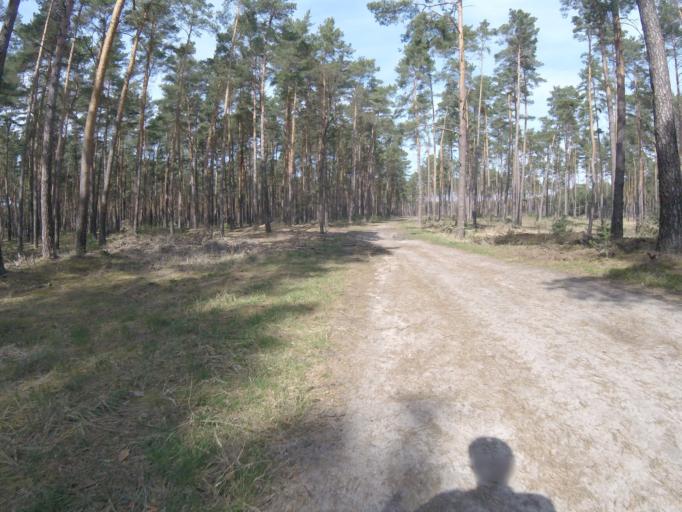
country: DE
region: Brandenburg
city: Gross Koris
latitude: 52.2034
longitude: 13.6646
